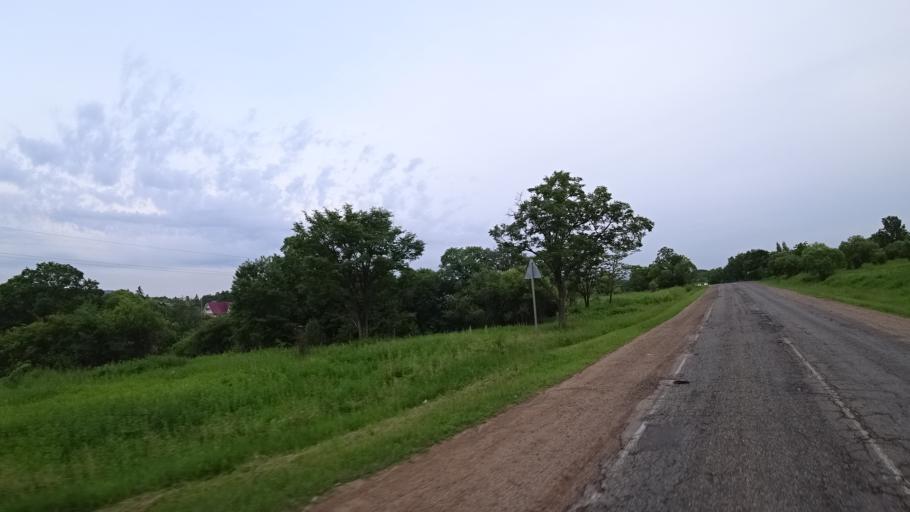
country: RU
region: Primorskiy
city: Novosysoyevka
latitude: 44.2240
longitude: 133.3506
